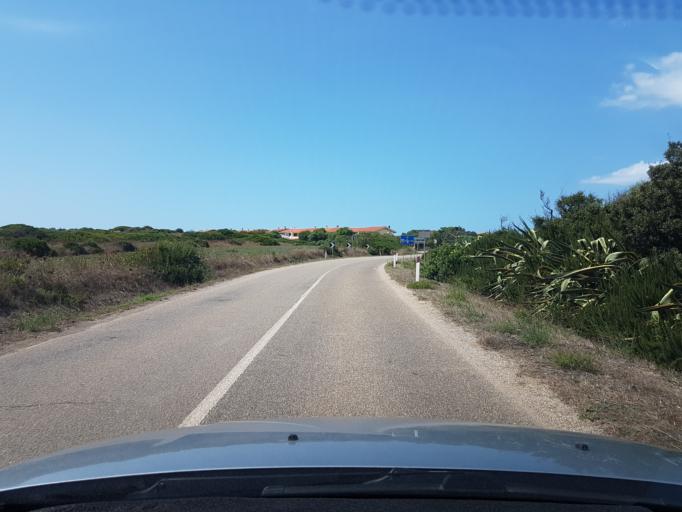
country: IT
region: Sardinia
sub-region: Provincia di Oristano
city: Riola Sardo
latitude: 40.0379
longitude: 8.4184
